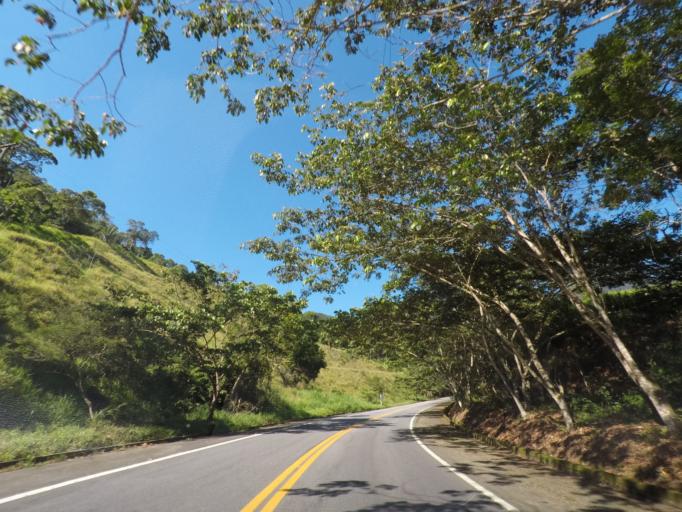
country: BR
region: Rio de Janeiro
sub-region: Parati
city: Paraty
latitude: -23.3419
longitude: -44.7374
